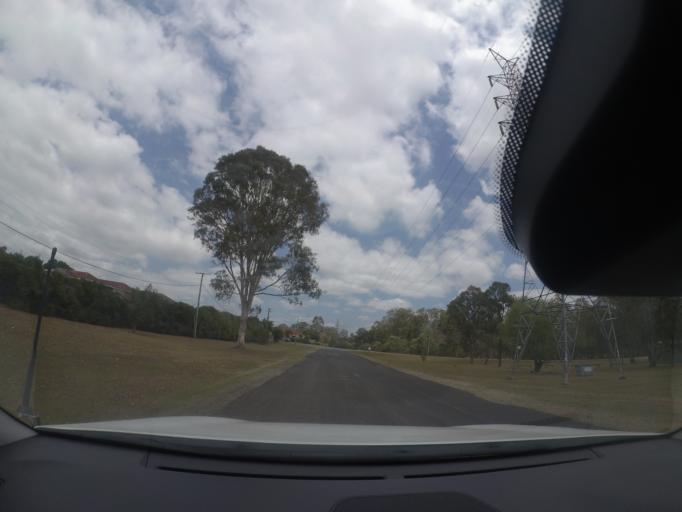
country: AU
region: Queensland
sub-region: Logan
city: Slacks Creek
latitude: -27.6572
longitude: 153.1468
